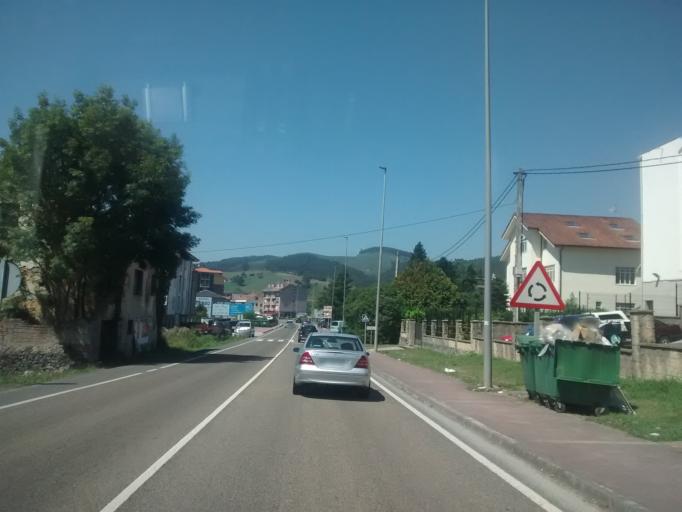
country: ES
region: Cantabria
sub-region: Provincia de Cantabria
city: Hazas de Cesto
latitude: 43.4151
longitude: -3.5728
